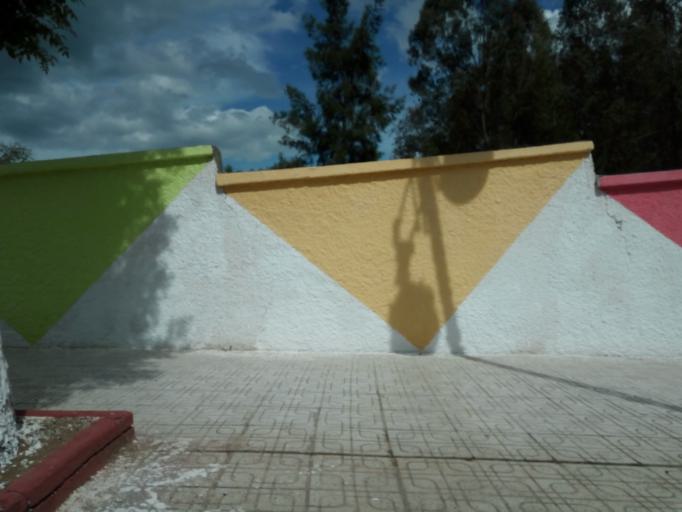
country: DZ
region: Constantine
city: Constantine
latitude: 36.3524
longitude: 6.6087
